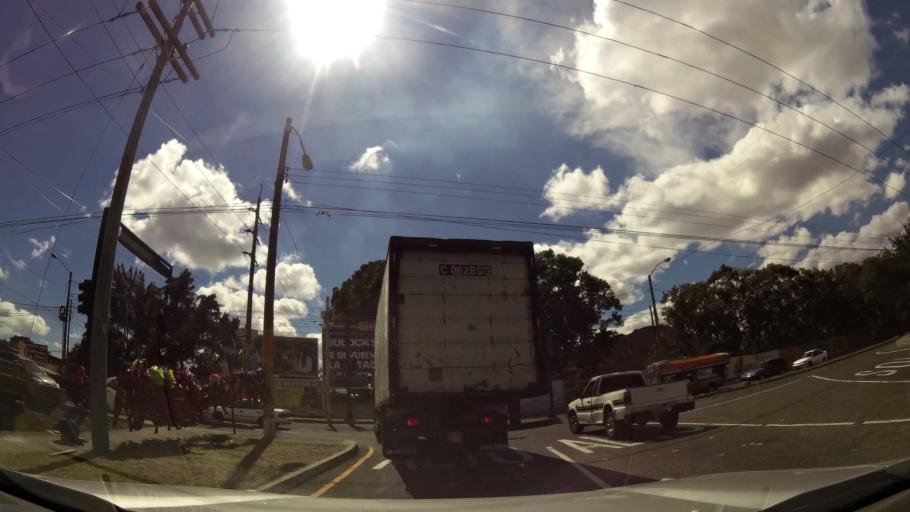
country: GT
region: Guatemala
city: Villa Nueva
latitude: 14.5569
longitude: -90.5486
